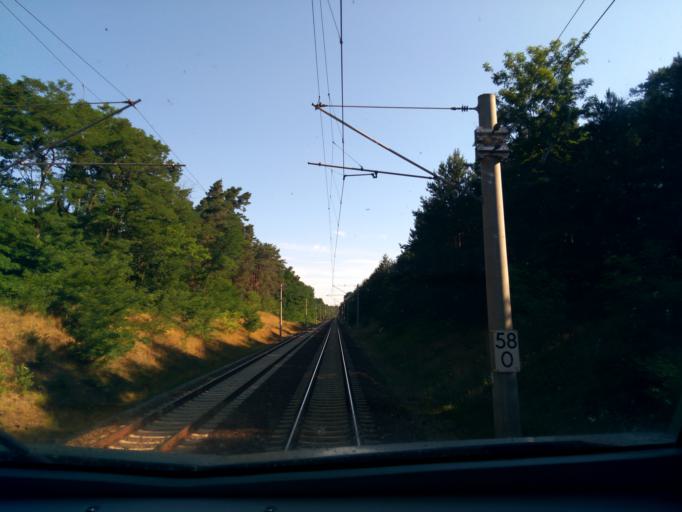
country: DE
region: Brandenburg
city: Halbe
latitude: 52.0452
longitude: 13.7198
